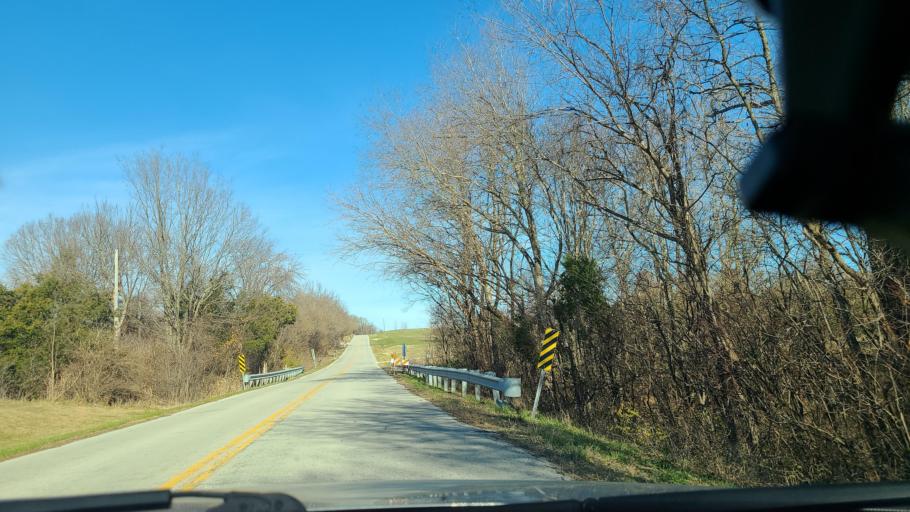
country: US
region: Kansas
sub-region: Leavenworth County
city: Lansing
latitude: 39.1934
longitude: -94.8639
